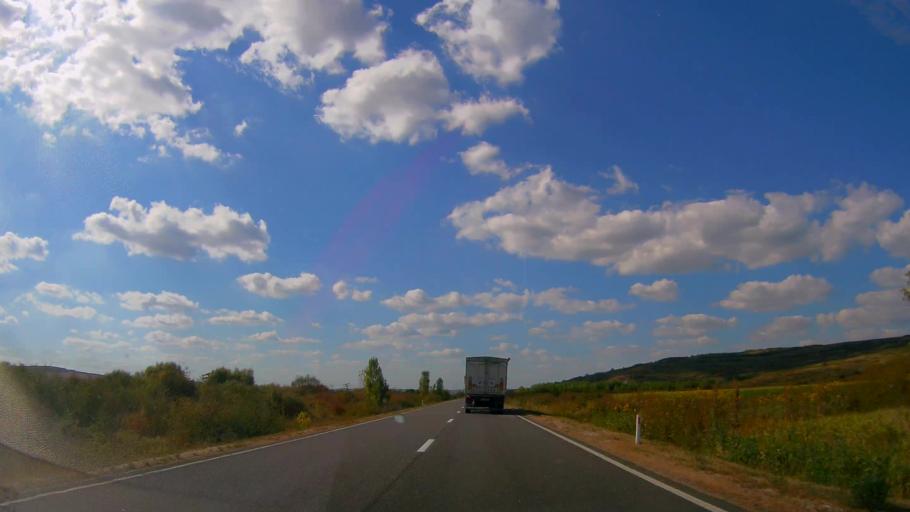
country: RO
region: Salaj
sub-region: Comuna Bocsa
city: Bocsa
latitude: 47.3244
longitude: 22.8812
